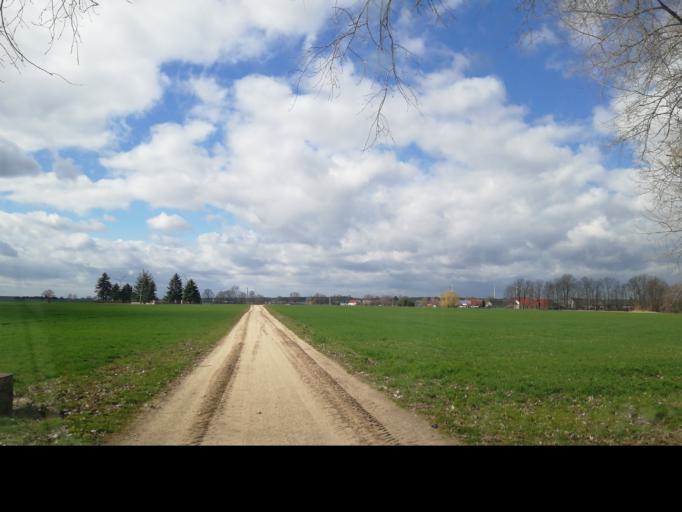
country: DE
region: Brandenburg
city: Schonewalde
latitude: 51.6869
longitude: 13.5418
